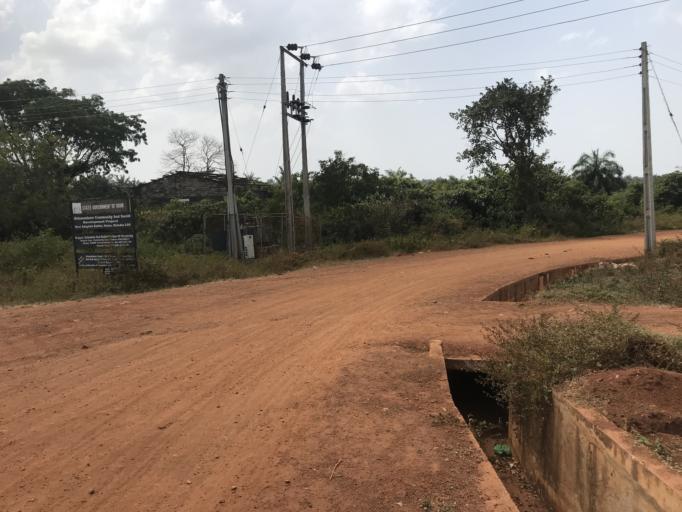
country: NG
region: Osun
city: Ikirun
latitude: 7.9356
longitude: 4.6396
